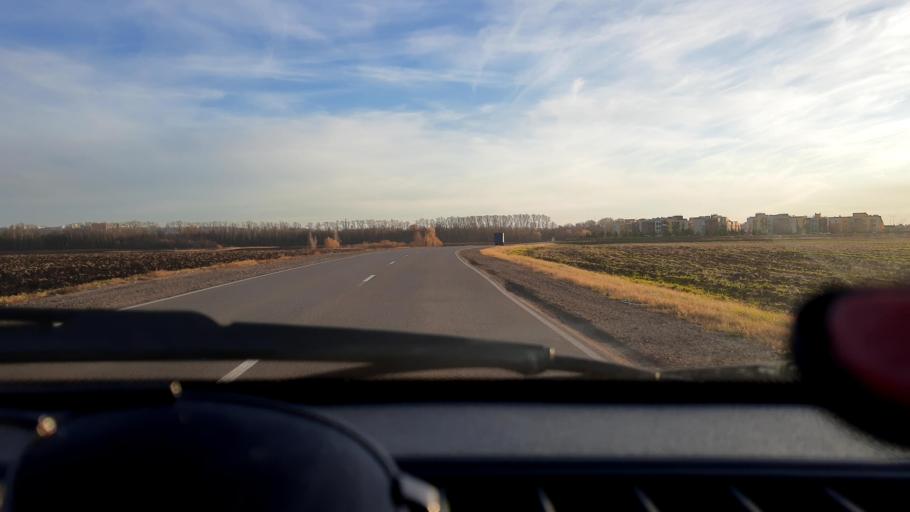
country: RU
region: Bashkortostan
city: Ufa
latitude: 54.8027
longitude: 55.9637
